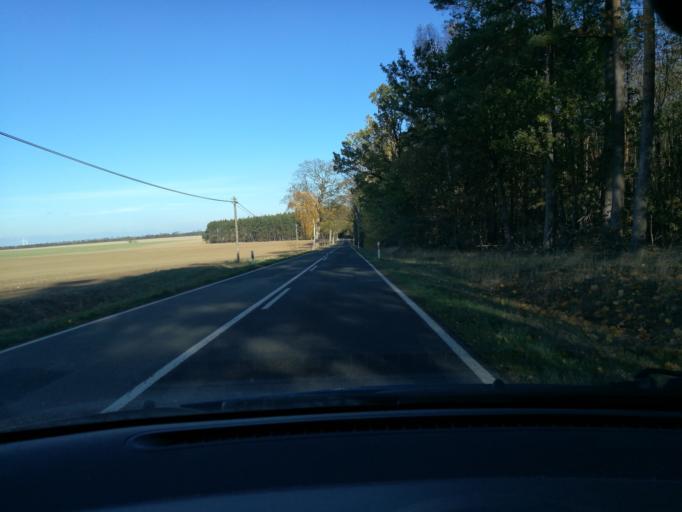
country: DE
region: Brandenburg
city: Lanz
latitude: 53.1387
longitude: 11.5636
